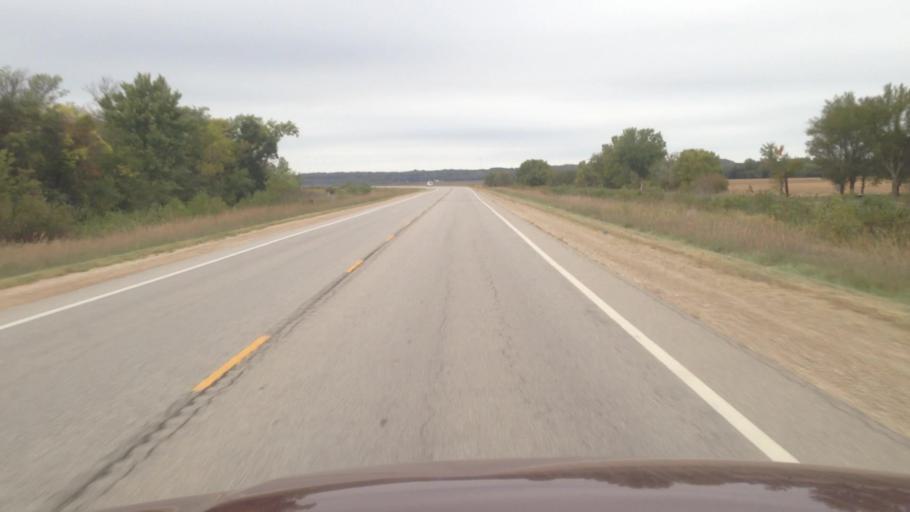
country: US
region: Kansas
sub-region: Jefferson County
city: Oskaloosa
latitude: 39.0843
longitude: -95.4097
